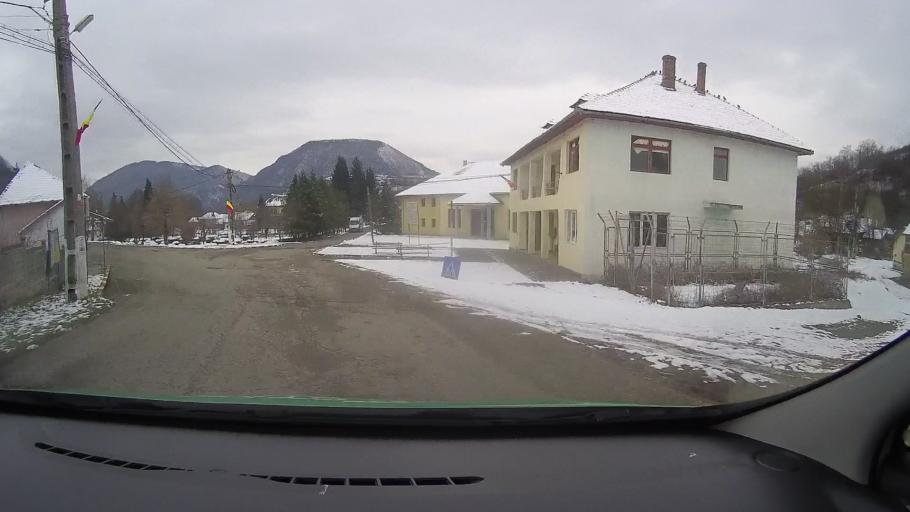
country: RO
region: Hunedoara
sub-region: Comuna Balsa
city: Balsa
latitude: 46.0286
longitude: 23.0995
